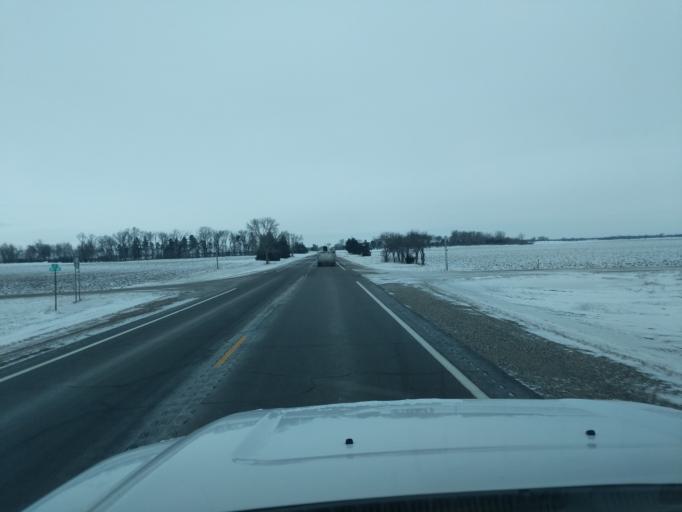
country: US
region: Minnesota
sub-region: Redwood County
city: Redwood Falls
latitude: 44.5930
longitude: -94.9944
